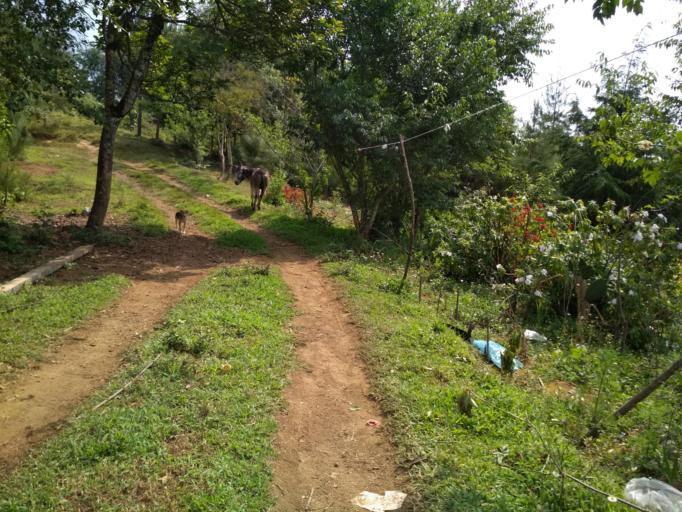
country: MX
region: Veracruz
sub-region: Camerino Z. Mendoza
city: Necoxtla
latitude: 18.7649
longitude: -97.1450
